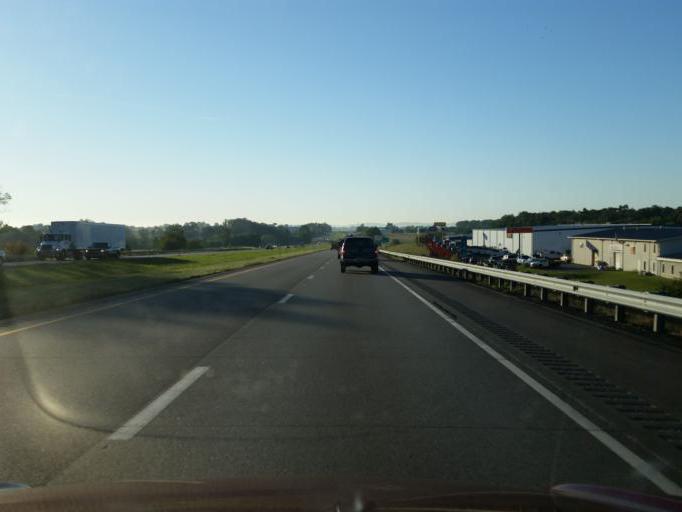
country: US
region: Pennsylvania
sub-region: Lancaster County
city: Rheems
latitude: 40.1483
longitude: -76.5624
